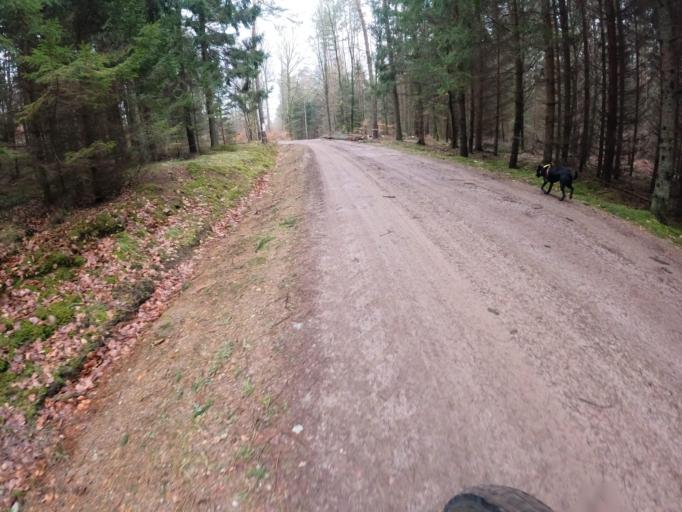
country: PL
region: West Pomeranian Voivodeship
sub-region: Powiat koszalinski
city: Polanow
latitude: 54.2333
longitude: 16.6771
